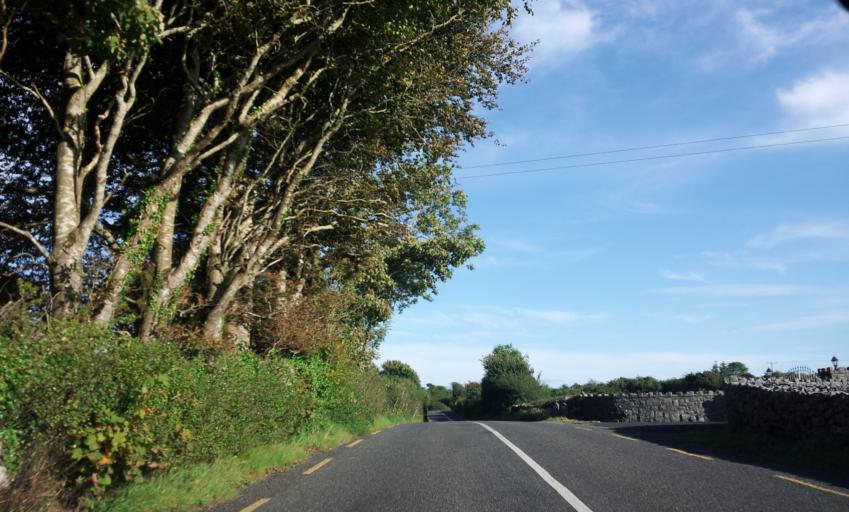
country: IE
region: Munster
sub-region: An Clar
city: Ennis
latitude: 52.9762
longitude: -9.1010
